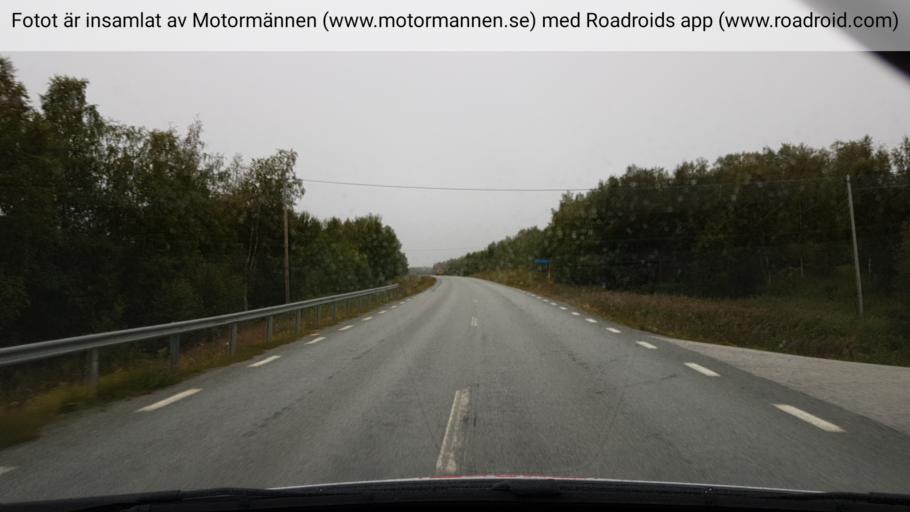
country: NO
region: Nordland
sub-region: Rana
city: Mo i Rana
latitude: 65.7909
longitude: 15.1037
